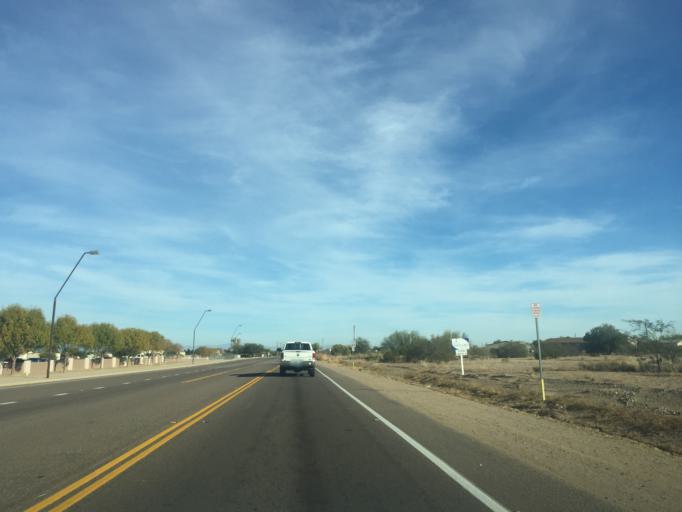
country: US
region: Arizona
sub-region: Maricopa County
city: Queen Creek
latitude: 33.2194
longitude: -111.6683
